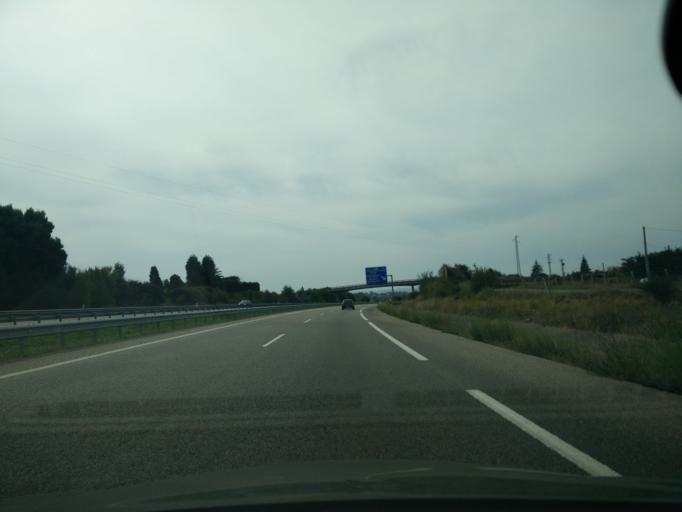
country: ES
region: Asturias
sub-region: Province of Asturias
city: Arriba
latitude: 43.5086
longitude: -5.5577
